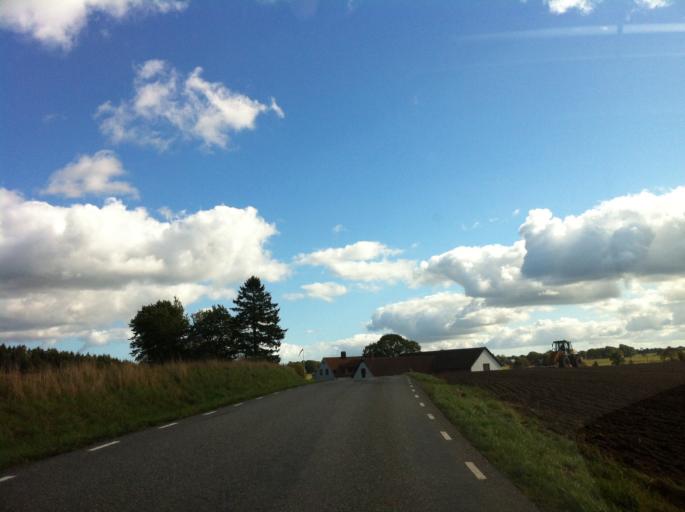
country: SE
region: Skane
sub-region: Kristianstads Kommun
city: Degeberga
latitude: 55.7058
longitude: 14.0045
